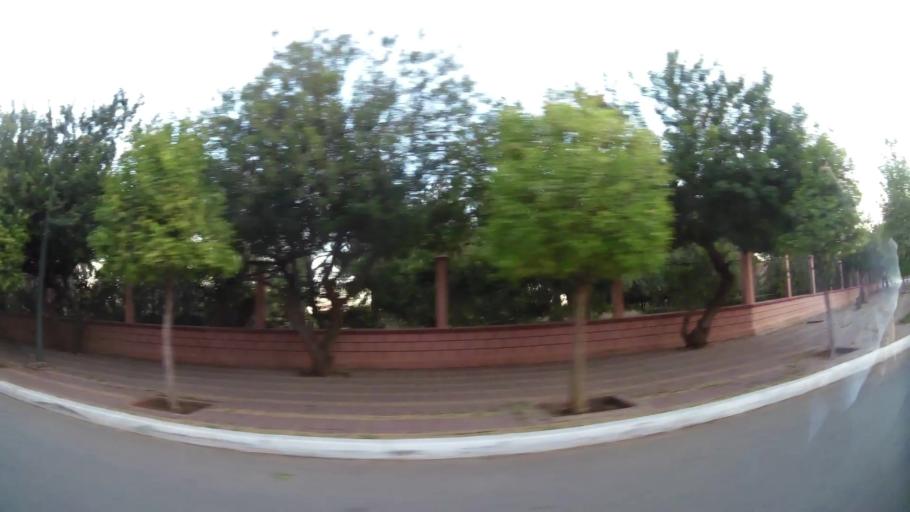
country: MA
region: Marrakech-Tensift-Al Haouz
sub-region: Kelaa-Des-Sraghna
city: Sidi Bou Othmane
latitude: 32.2142
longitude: -7.9270
